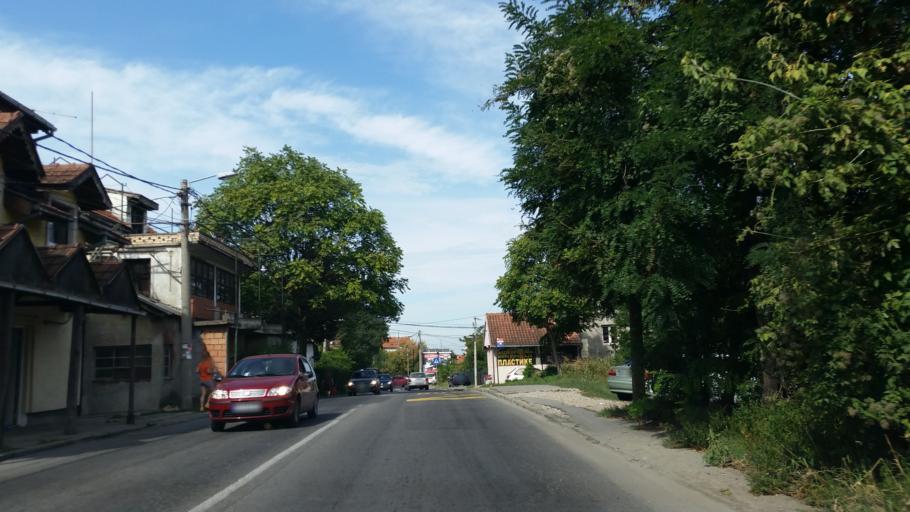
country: RS
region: Central Serbia
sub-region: Belgrade
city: Palilula
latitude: 44.8104
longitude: 20.5106
